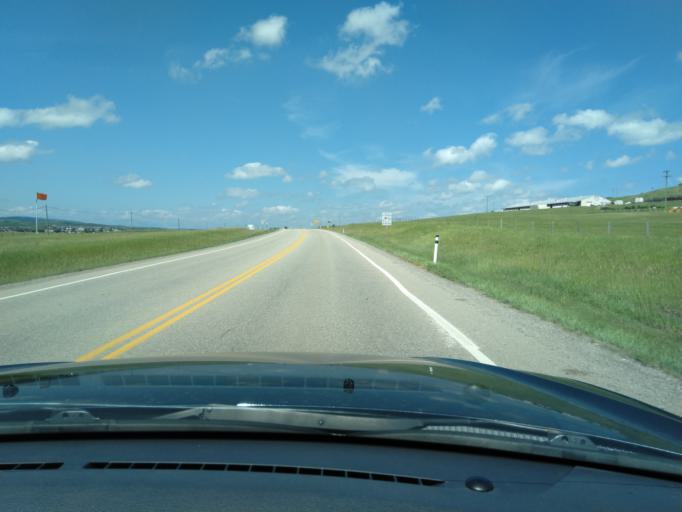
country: CA
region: Alberta
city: Cochrane
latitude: 51.2001
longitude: -114.4901
